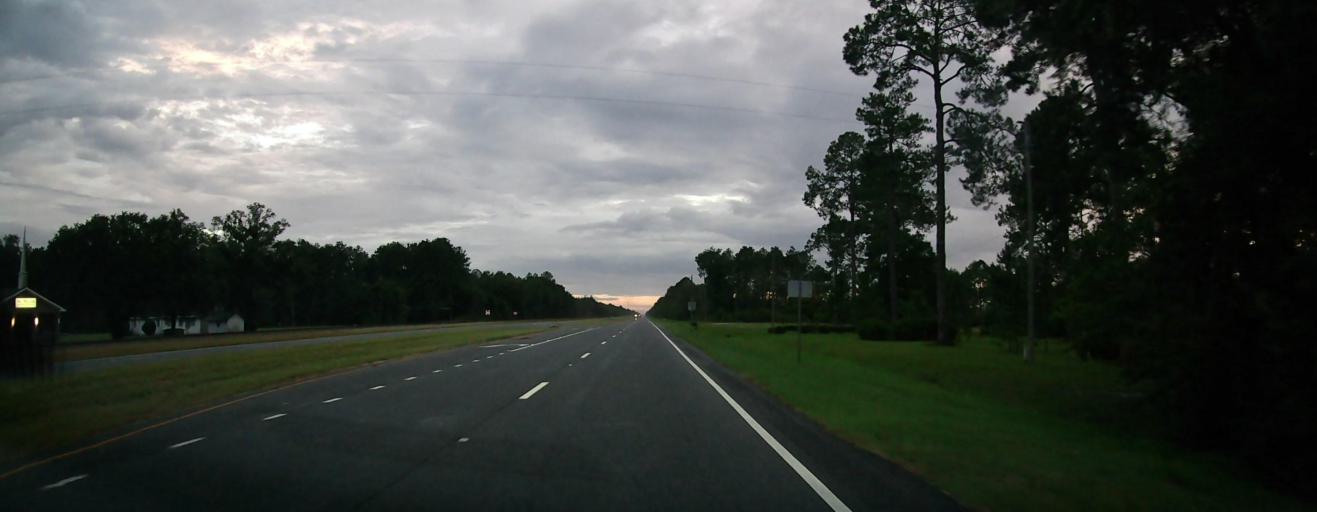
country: US
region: Georgia
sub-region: Lowndes County
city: Valdosta
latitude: 30.8842
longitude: -83.1403
